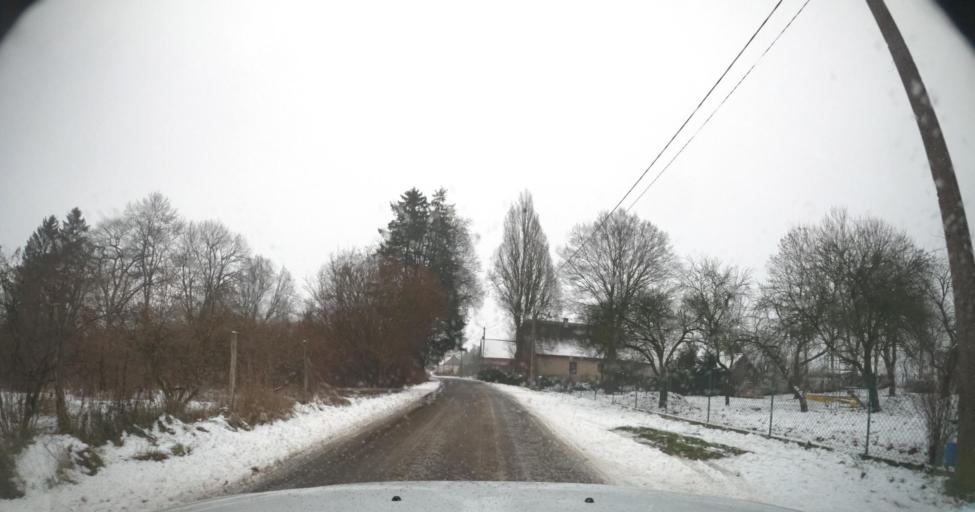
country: PL
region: West Pomeranian Voivodeship
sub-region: Powiat kamienski
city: Golczewo
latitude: 53.7896
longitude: 14.9555
